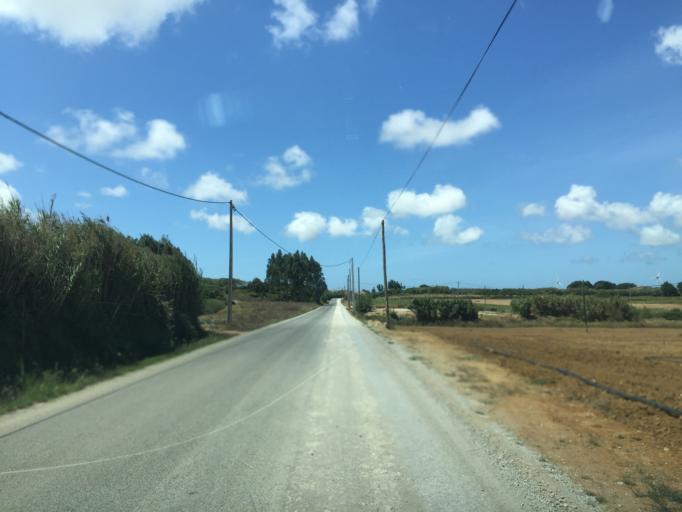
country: PT
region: Lisbon
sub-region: Lourinha
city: Lourinha
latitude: 39.2785
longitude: -9.2489
